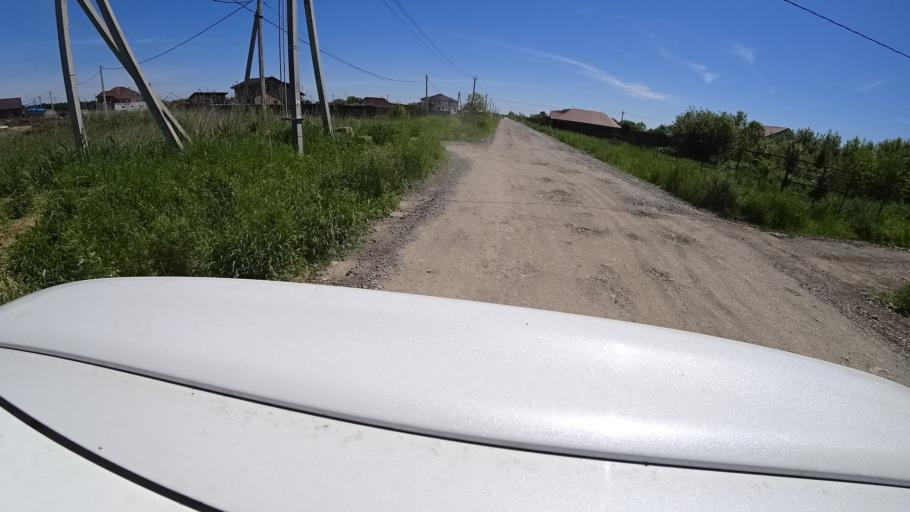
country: RU
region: Khabarovsk Krai
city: Topolevo
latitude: 48.5112
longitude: 135.1938
